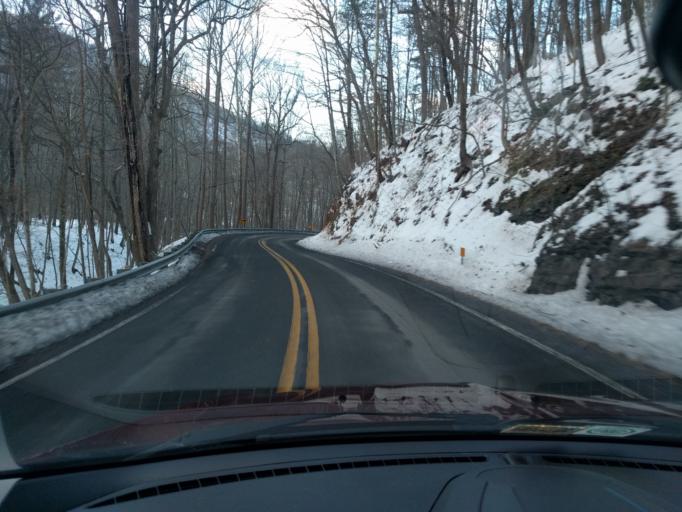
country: US
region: Virginia
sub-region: Bath County
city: Warm Springs
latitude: 38.0708
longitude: -79.8840
